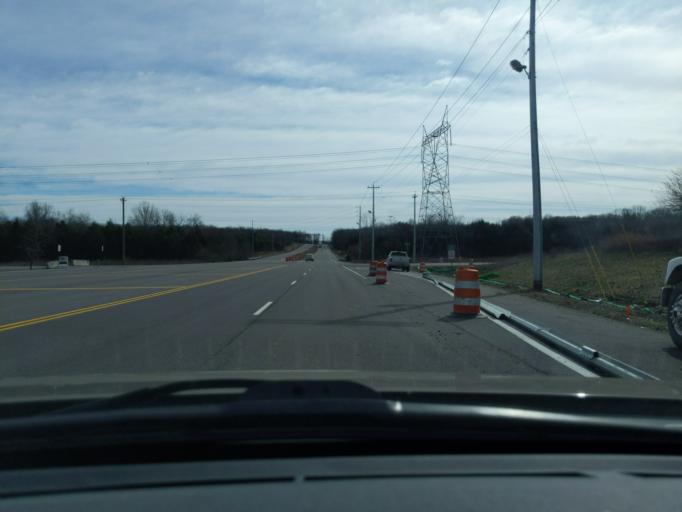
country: US
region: Tennessee
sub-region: Wilson County
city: Mount Juliet
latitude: 36.1860
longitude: -86.4645
